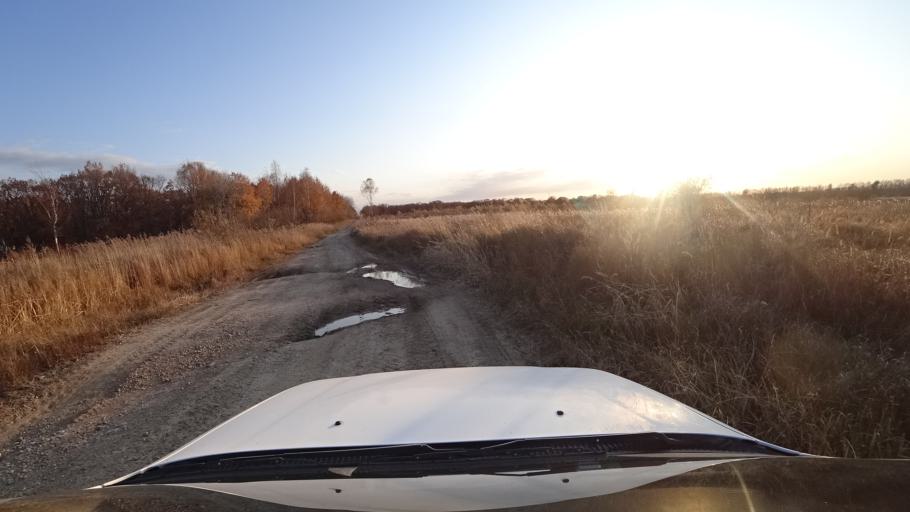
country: RU
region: Primorskiy
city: Lazo
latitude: 45.8077
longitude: 133.6063
